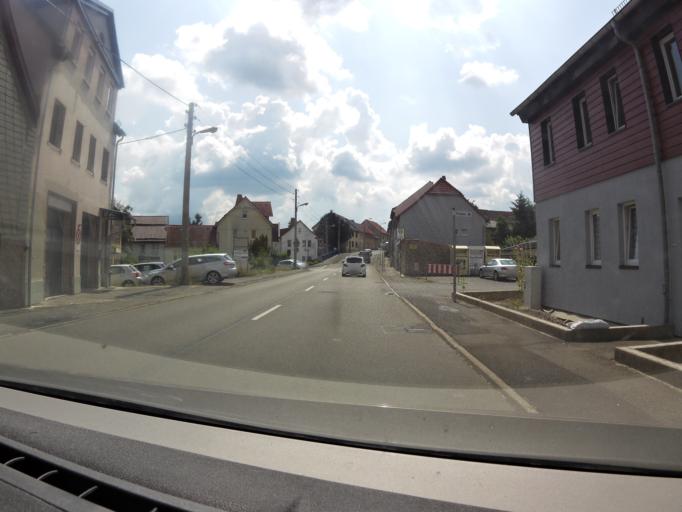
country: DE
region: Thuringia
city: Plaue
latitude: 50.7803
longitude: 10.9000
